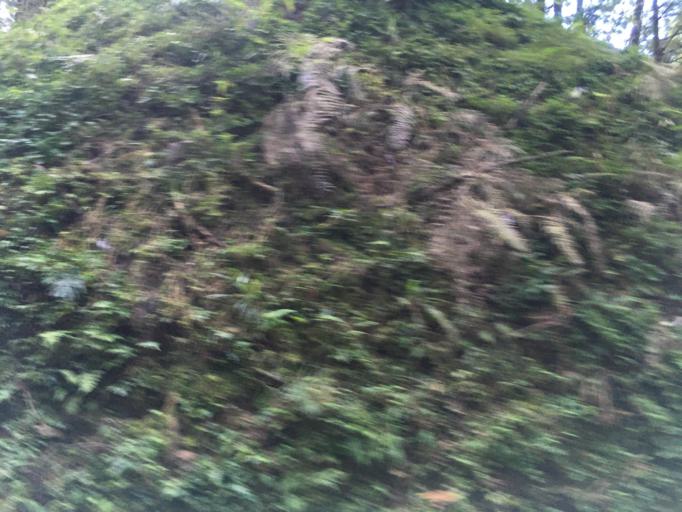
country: TW
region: Taiwan
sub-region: Yilan
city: Yilan
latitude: 24.6175
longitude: 121.4812
